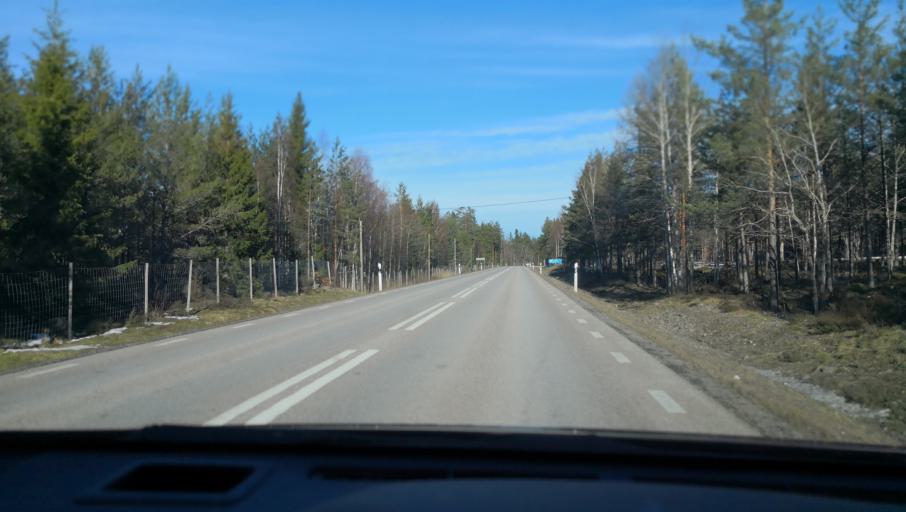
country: SE
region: Uppsala
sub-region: Uppsala Kommun
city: Vattholma
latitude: 60.1068
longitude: 17.7792
